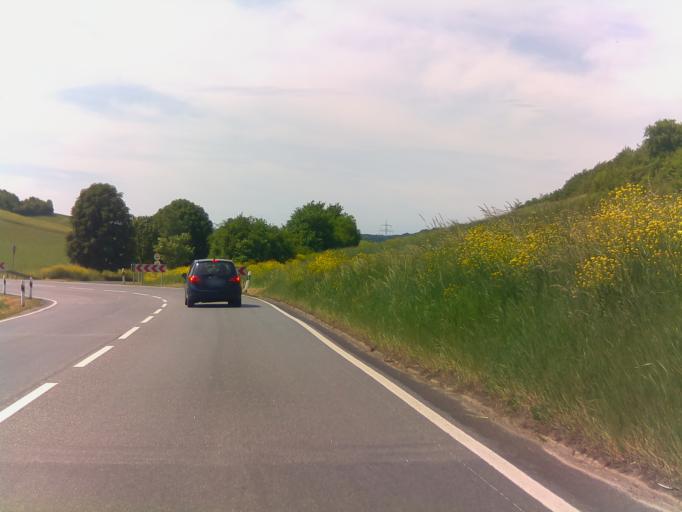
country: DE
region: Bavaria
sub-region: Regierungsbezirk Unterfranken
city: Arnstein
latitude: 49.9771
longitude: 9.9350
